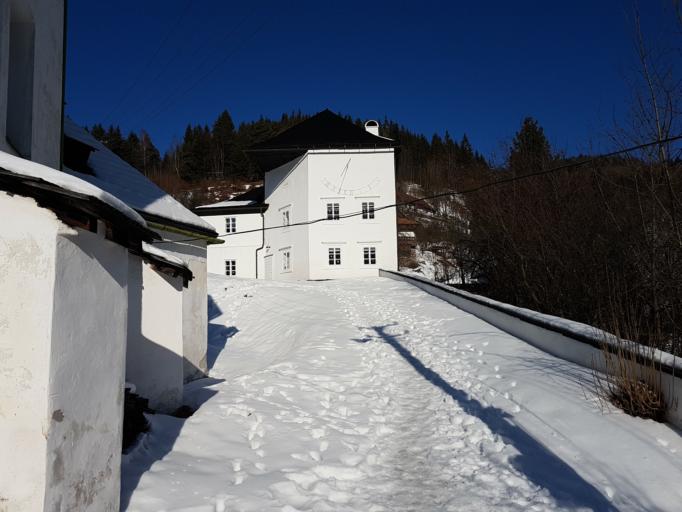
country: SK
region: Banskobystricky
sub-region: Okres Banska Bystrica
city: Banska Bystrica
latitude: 48.8083
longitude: 19.1331
